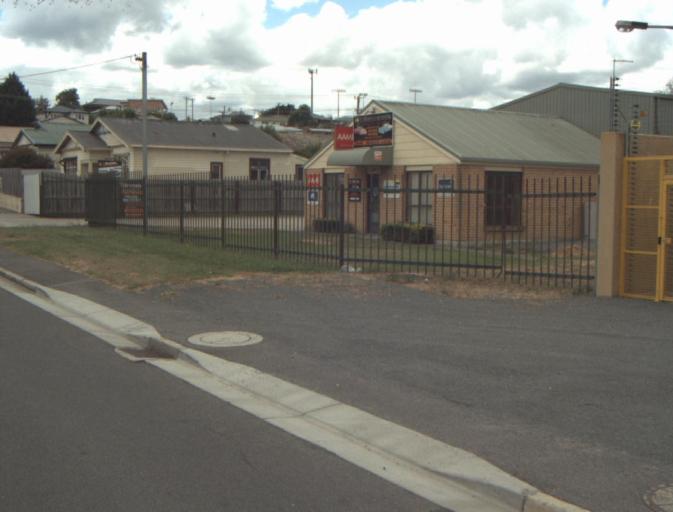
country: AU
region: Tasmania
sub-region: Launceston
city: Newnham
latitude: -41.4092
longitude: 147.1358
